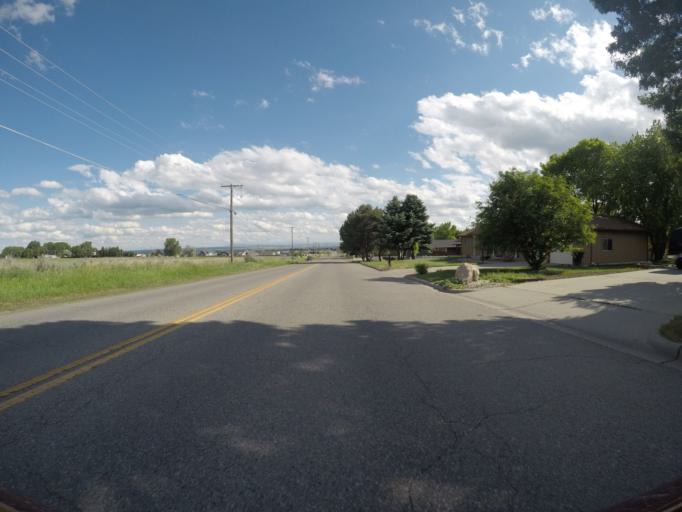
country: US
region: Montana
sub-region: Yellowstone County
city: Billings
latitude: 45.8010
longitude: -108.6527
